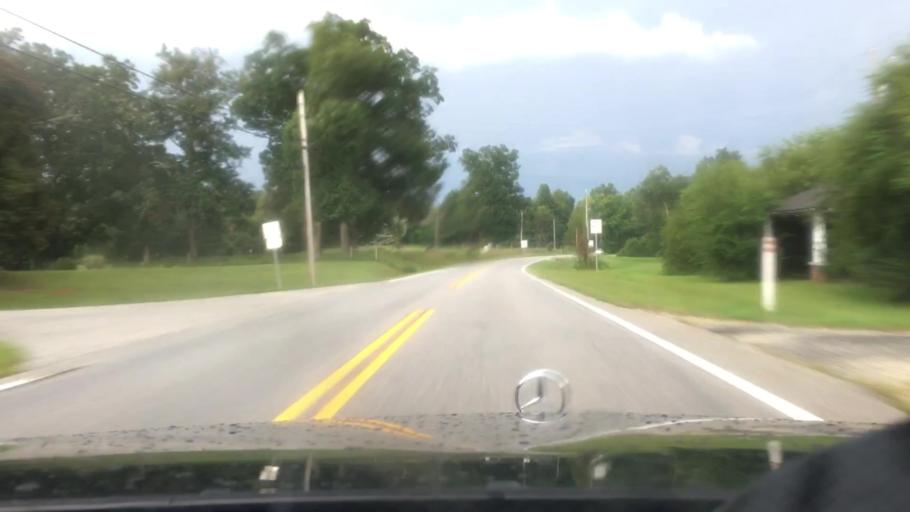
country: US
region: Virginia
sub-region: Nelson County
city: Lovingston
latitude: 37.7693
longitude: -78.9797
